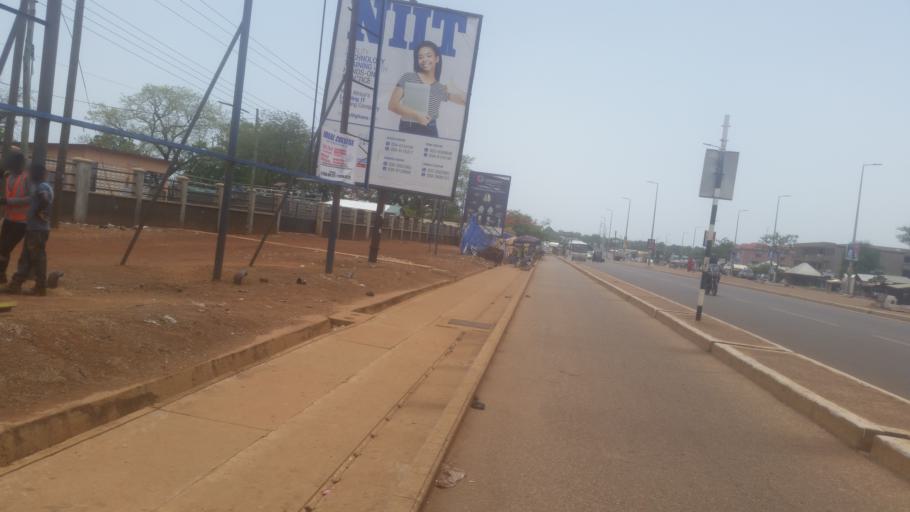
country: GH
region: Northern
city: Tamale
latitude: 9.3944
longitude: -0.8233
